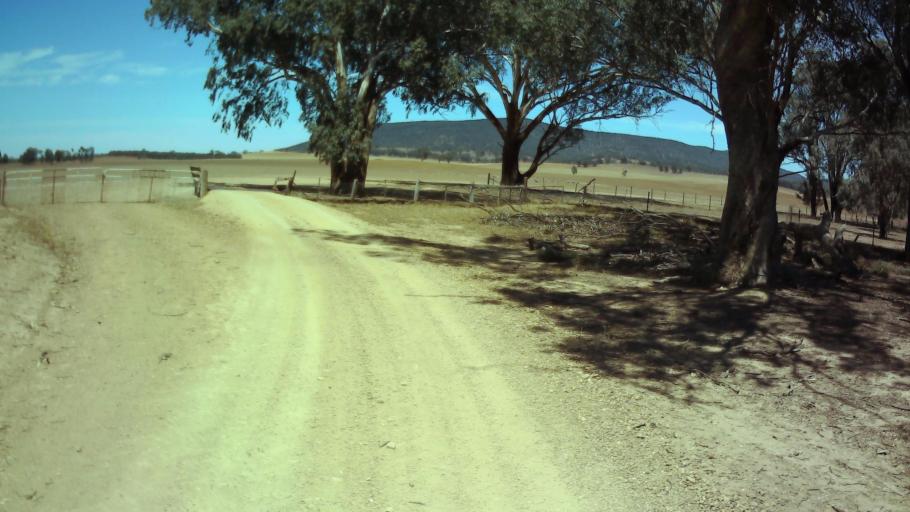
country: AU
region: New South Wales
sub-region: Weddin
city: Grenfell
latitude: -33.9679
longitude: 148.1320
